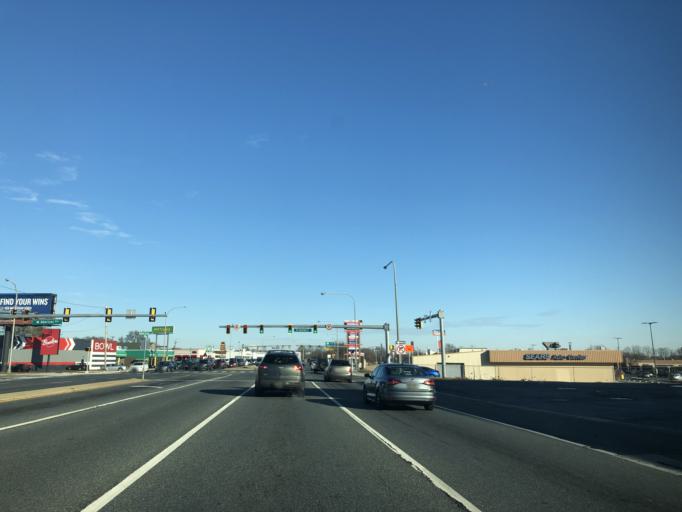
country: US
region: Delaware
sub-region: New Castle County
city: Newport
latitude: 39.7367
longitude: -75.6277
